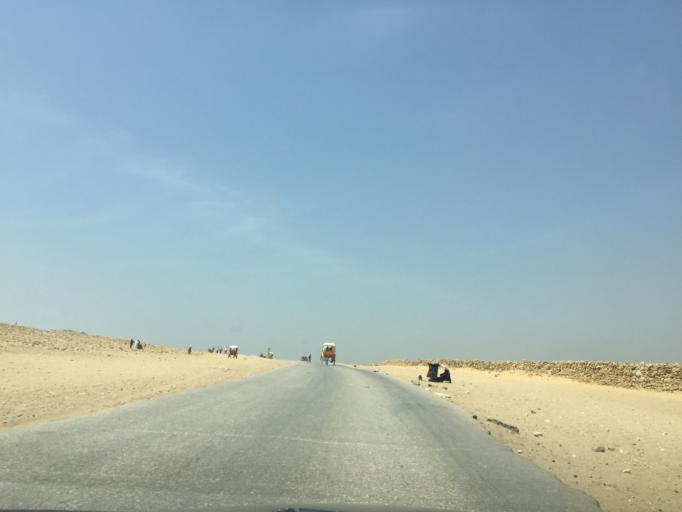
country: EG
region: Al Jizah
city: Al Jizah
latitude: 29.9751
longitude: 31.1283
